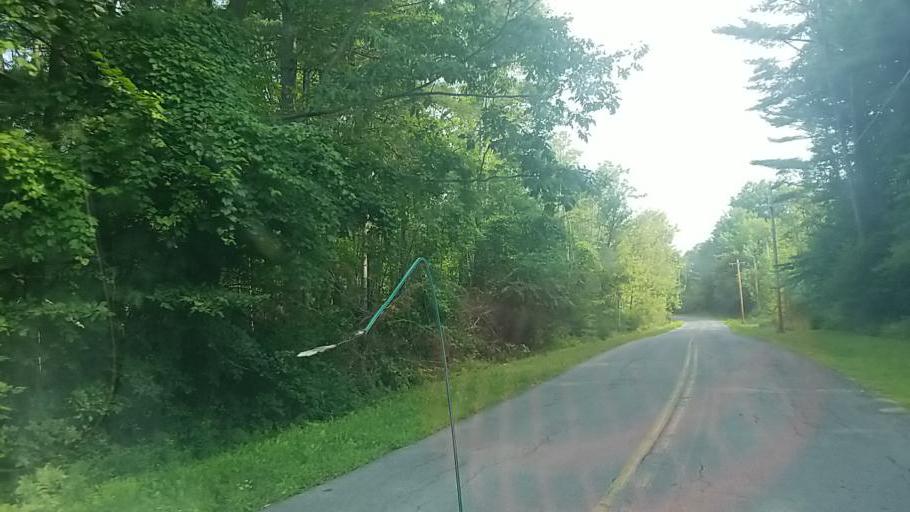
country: US
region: New York
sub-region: Fulton County
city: Broadalbin
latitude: 43.0762
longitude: -74.2238
